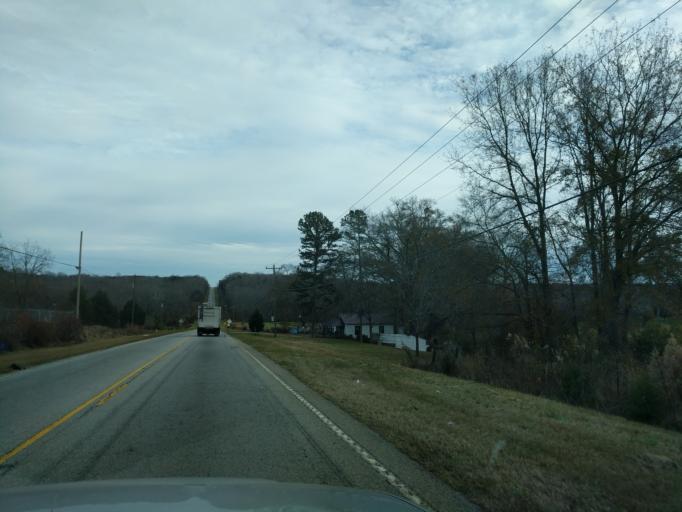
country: US
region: South Carolina
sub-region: Anderson County
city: Williamston
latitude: 34.6409
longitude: -82.4417
